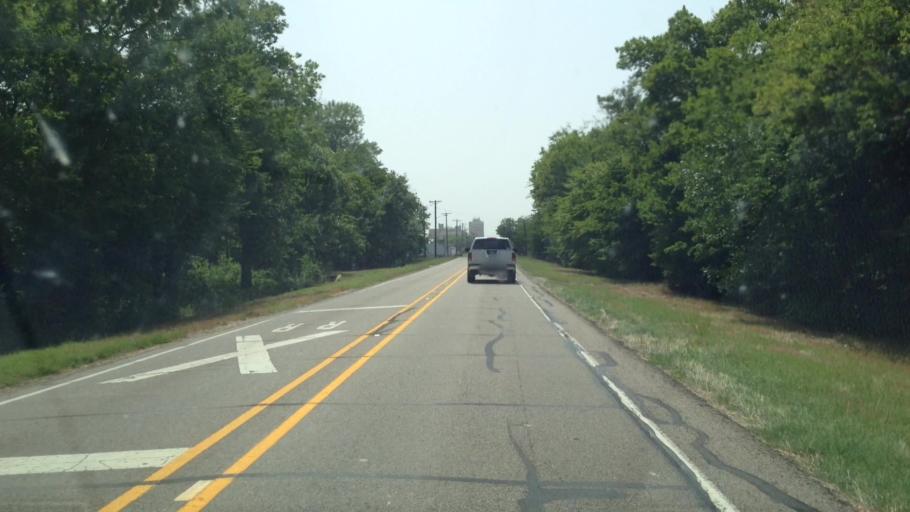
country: US
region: Texas
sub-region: Hunt County
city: Greenville
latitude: 33.1397
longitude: -96.0954
